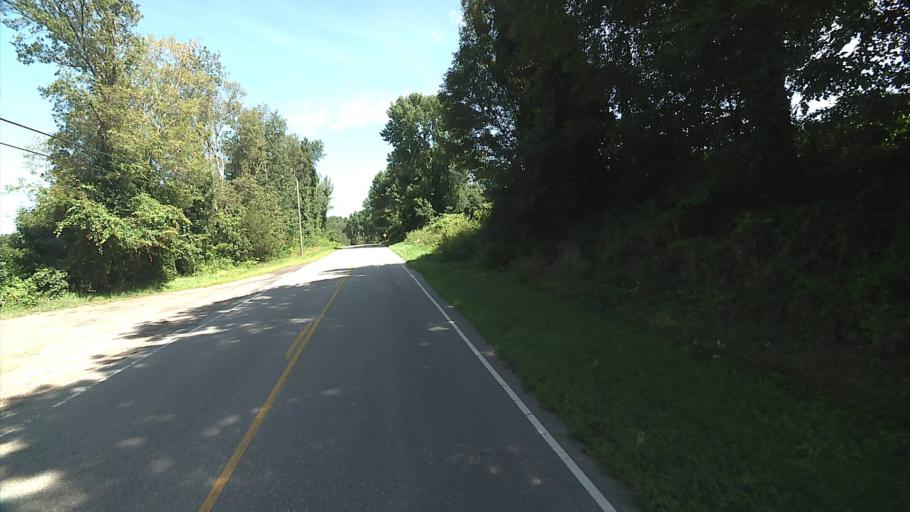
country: US
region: Connecticut
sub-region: New London County
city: Baltic
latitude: 41.6542
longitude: -72.0926
